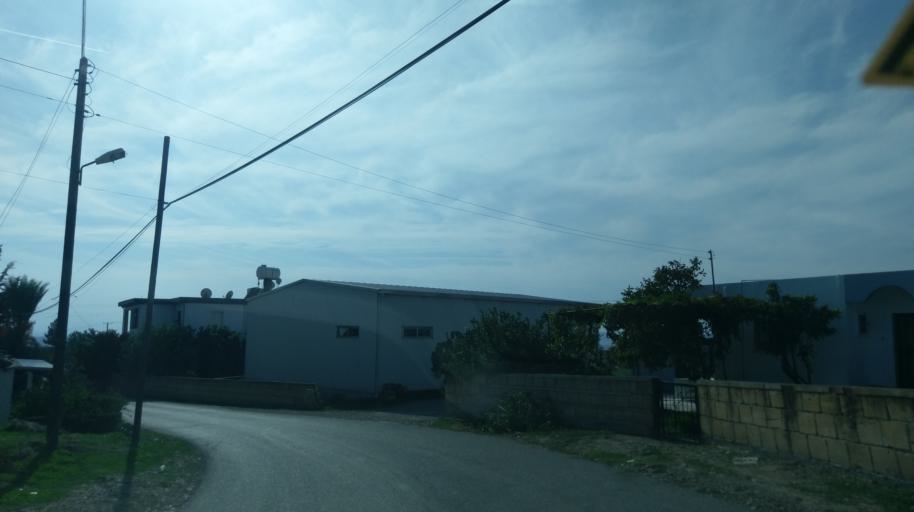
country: CY
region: Keryneia
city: Lapithos
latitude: 35.2699
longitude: 33.2253
